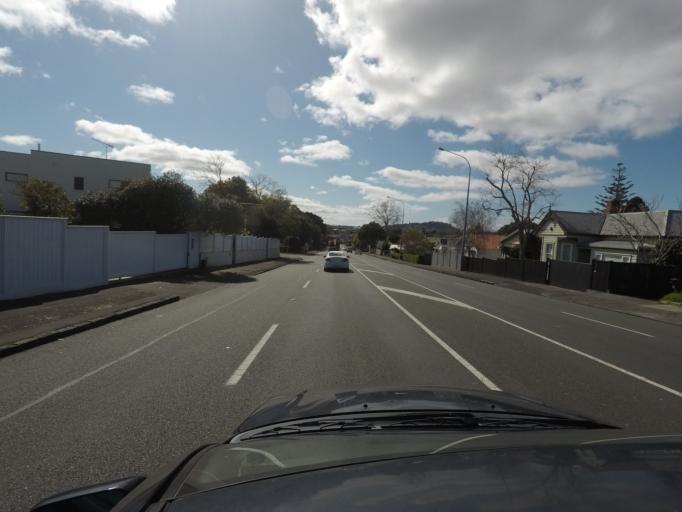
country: NZ
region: Auckland
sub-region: Auckland
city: Auckland
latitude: -36.8817
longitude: 174.7211
